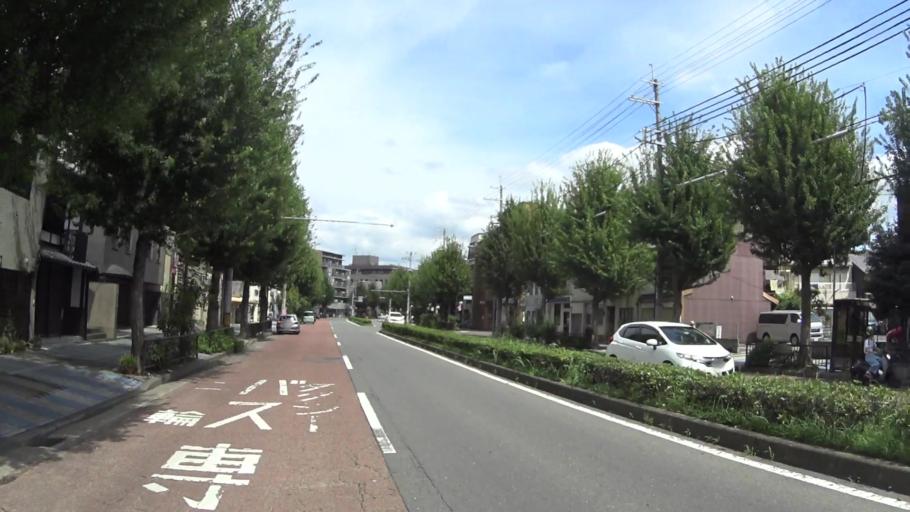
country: JP
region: Kyoto
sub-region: Kyoto-shi
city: Kamigyo-ku
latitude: 35.0428
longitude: 135.7554
